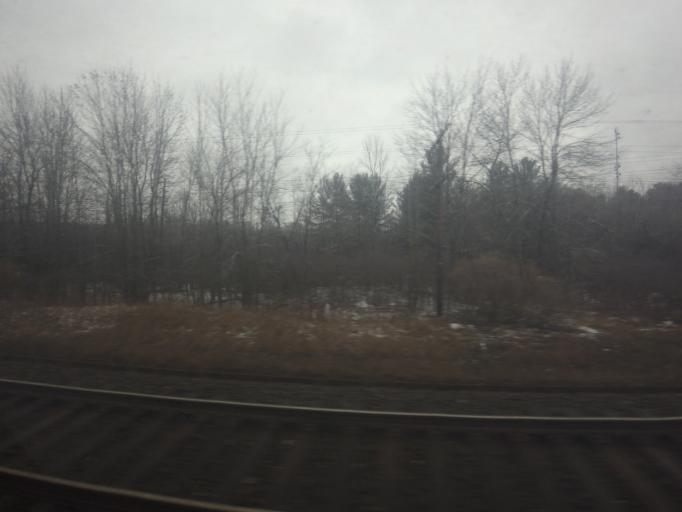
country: CA
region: Ontario
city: Kingston
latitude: 44.2934
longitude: -76.4320
